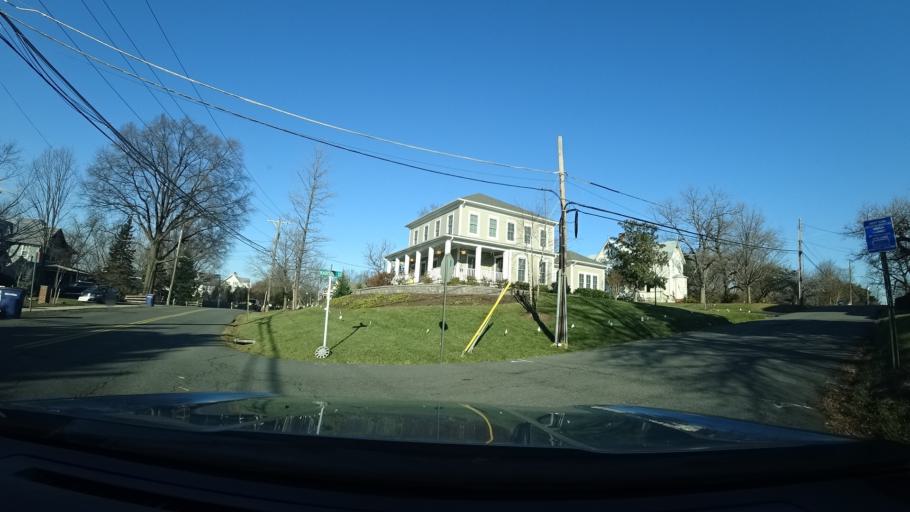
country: US
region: Virginia
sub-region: Fairfax County
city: Herndon
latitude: 38.9719
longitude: -77.3836
